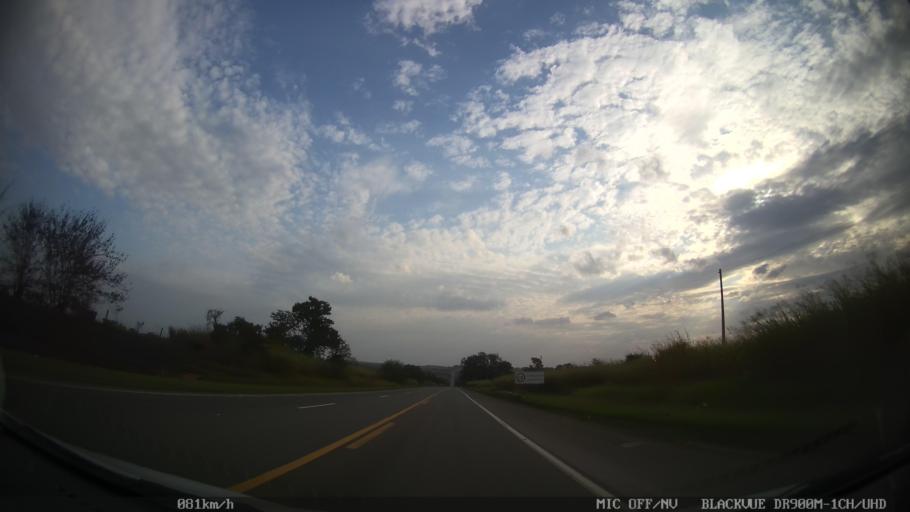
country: BR
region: Sao Paulo
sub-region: Cosmopolis
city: Cosmopolis
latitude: -22.6277
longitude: -47.2706
